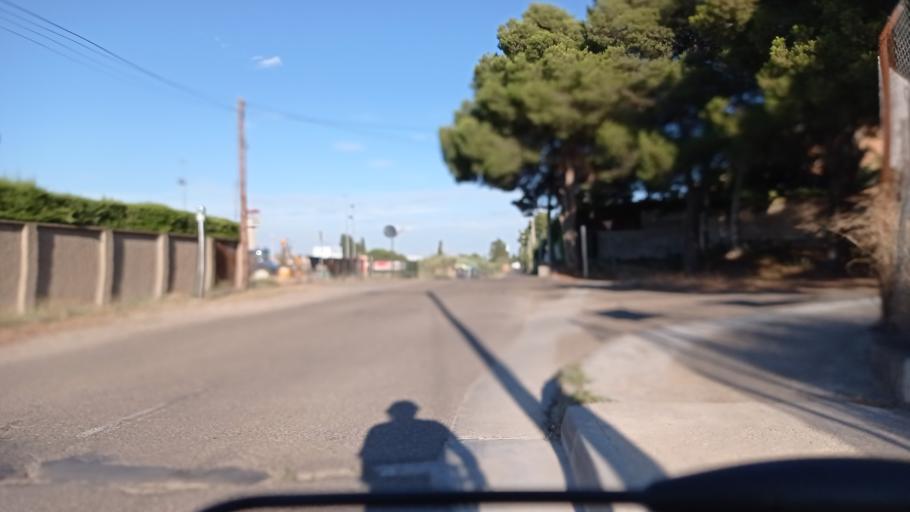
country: ES
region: Aragon
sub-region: Provincia de Zaragoza
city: Oliver-Valdefierro, Oliver, Valdefierro
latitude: 41.6745
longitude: -0.9571
